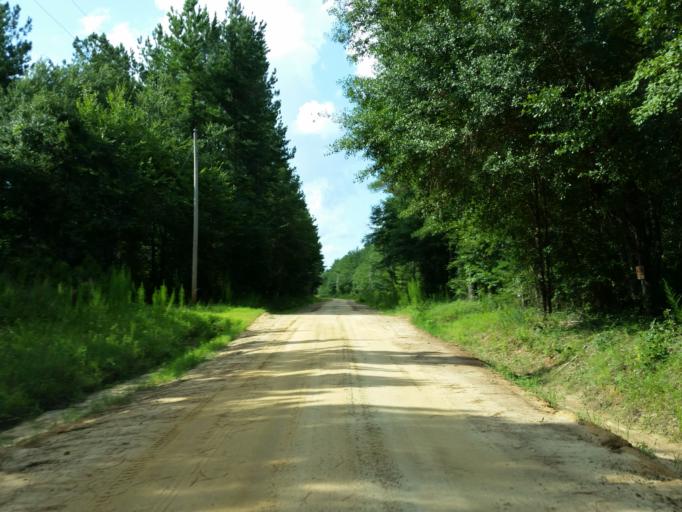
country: US
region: Georgia
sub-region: Lee County
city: Leesburg
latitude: 31.7686
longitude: -84.0186
